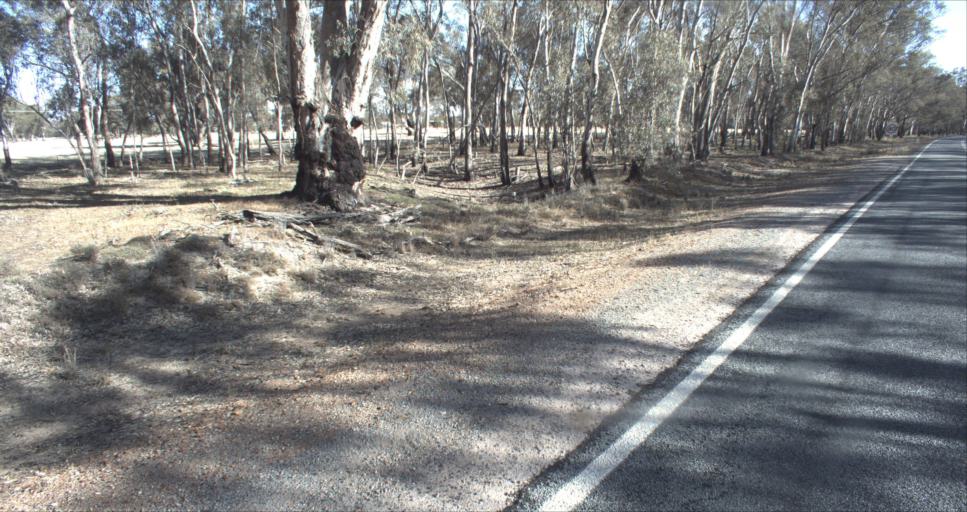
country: AU
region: New South Wales
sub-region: Leeton
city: Leeton
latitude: -34.6288
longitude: 146.3773
